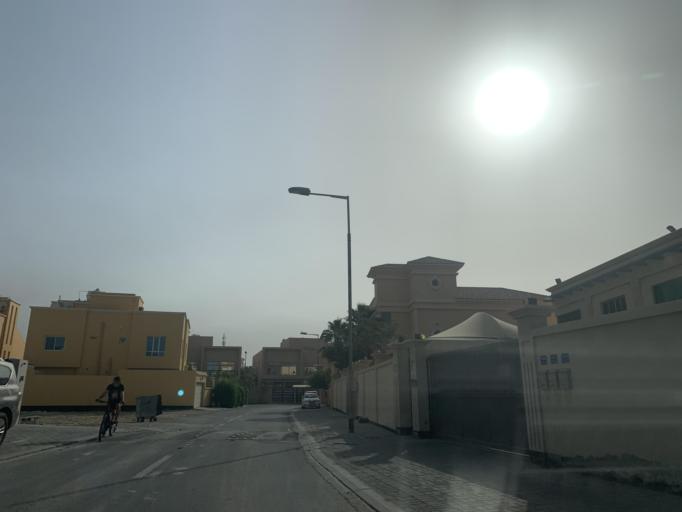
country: BH
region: Northern
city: Madinat `Isa
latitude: 26.1924
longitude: 50.5590
